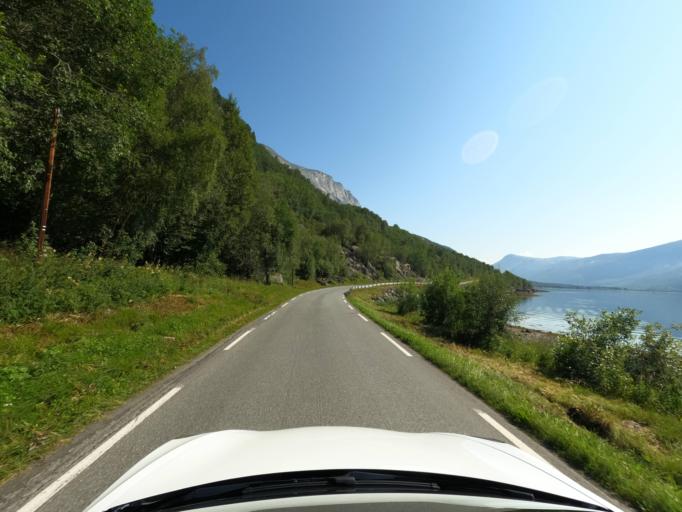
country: NO
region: Nordland
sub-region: Narvik
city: Narvik
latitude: 68.2797
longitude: 17.3854
